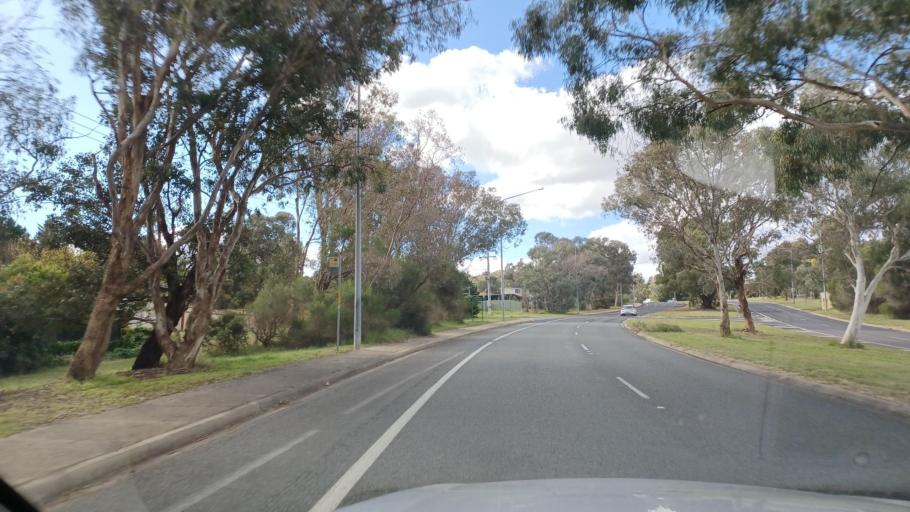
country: AU
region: Australian Capital Territory
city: Belconnen
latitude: -35.2072
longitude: 149.0478
